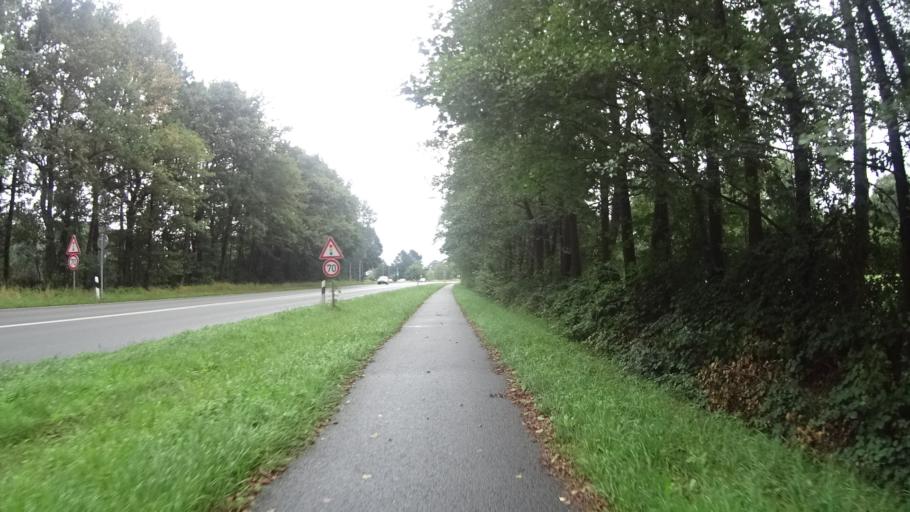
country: DE
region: Lower Saxony
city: Brinkum
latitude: 53.2655
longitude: 7.5466
